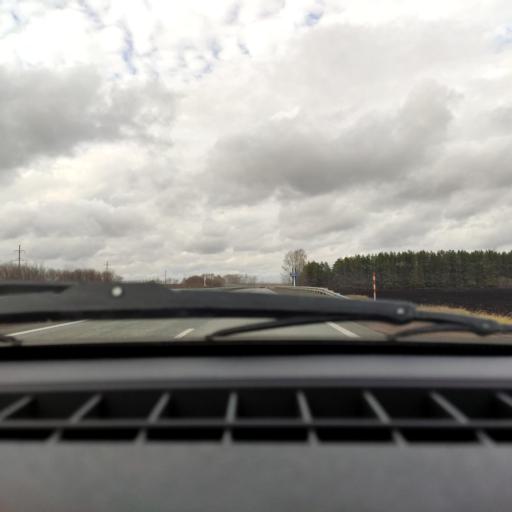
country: RU
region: Bashkortostan
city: Asanovo
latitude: 54.9180
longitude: 55.5864
